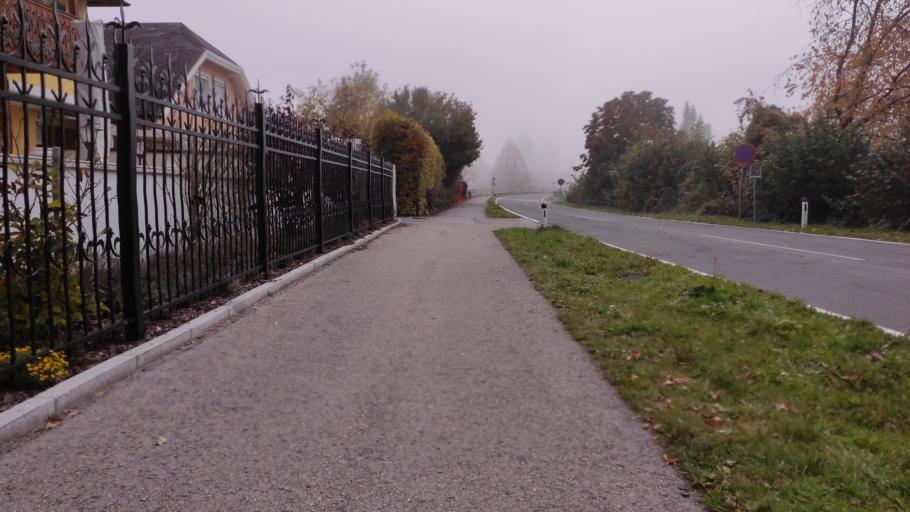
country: AT
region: Upper Austria
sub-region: Politischer Bezirk Gmunden
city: Sankt Wolfgang im Salzkammergut
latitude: 47.7261
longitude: 13.4384
